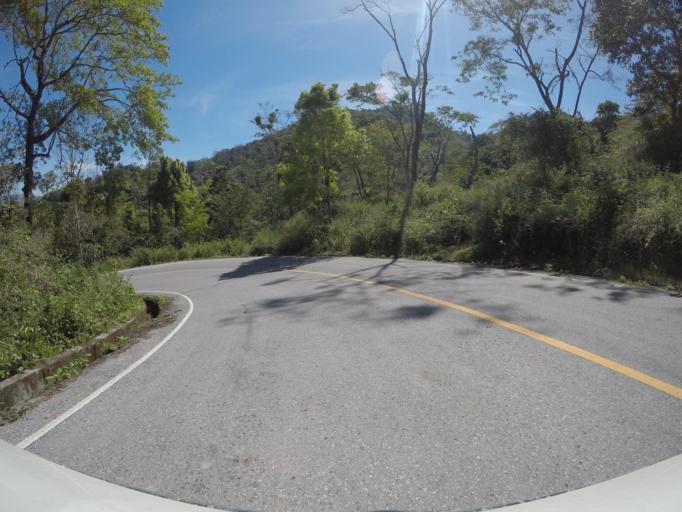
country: TL
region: Manufahi
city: Same
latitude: -8.9079
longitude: 125.9761
